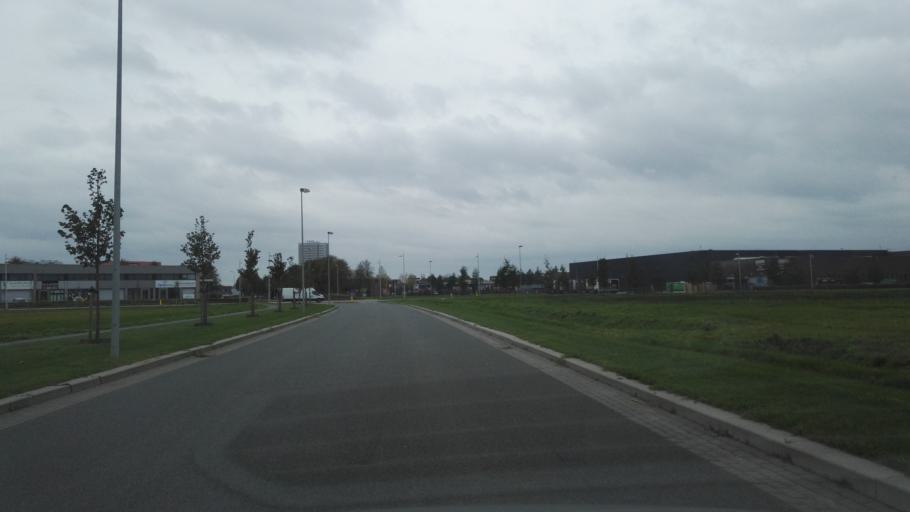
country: NL
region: Gelderland
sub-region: Gemeente Apeldoorn
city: Apeldoorn
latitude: 52.2445
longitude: 5.9934
